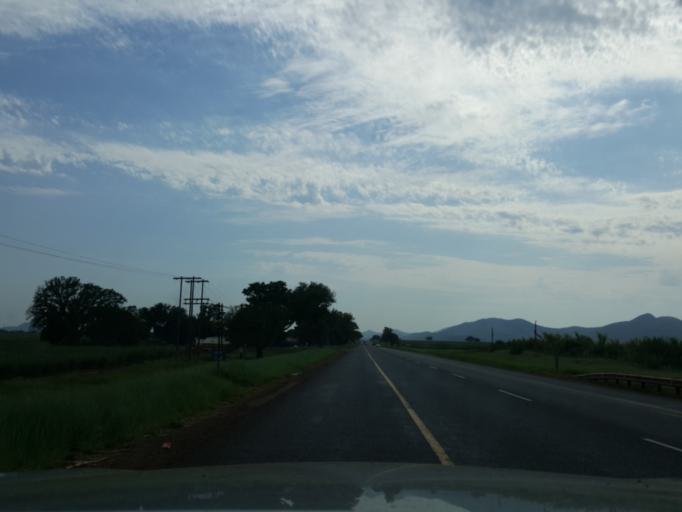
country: SZ
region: Hhohho
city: Ntfonjeni
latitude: -25.5082
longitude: 31.4818
